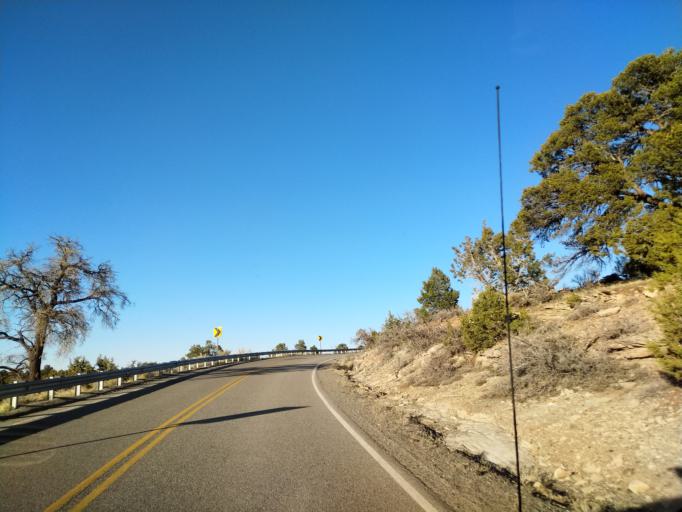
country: US
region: Colorado
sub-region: Mesa County
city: Redlands
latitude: 38.9919
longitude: -108.7728
